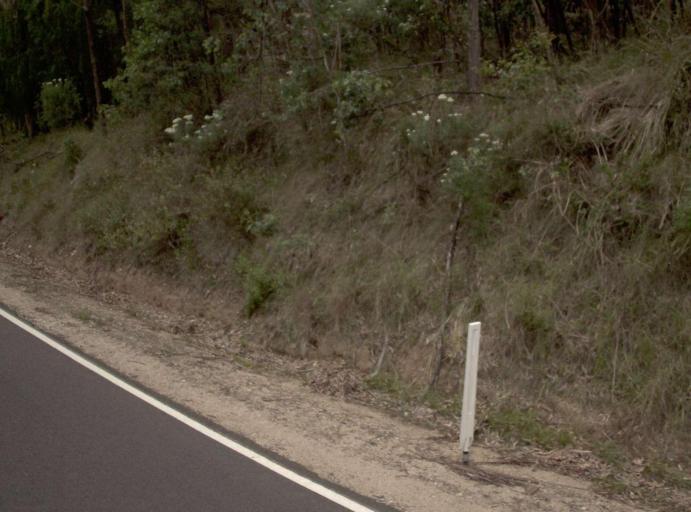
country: AU
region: New South Wales
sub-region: Bombala
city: Bombala
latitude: -37.4597
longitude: 149.1880
